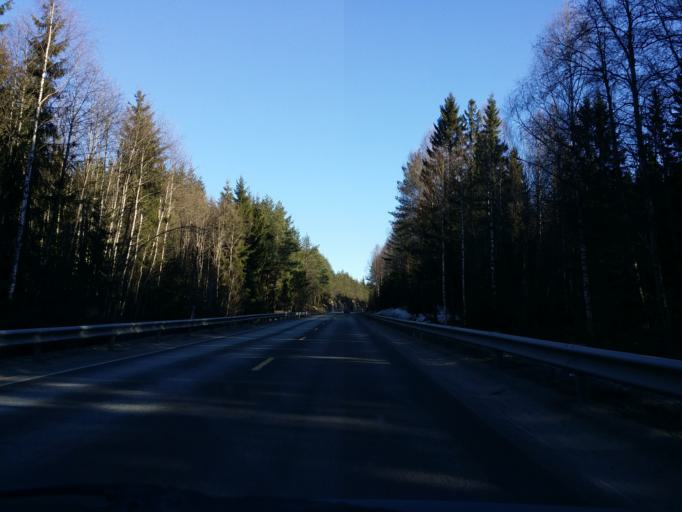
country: NO
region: Buskerud
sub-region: Ringerike
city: Honefoss
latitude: 60.2334
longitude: 10.2231
